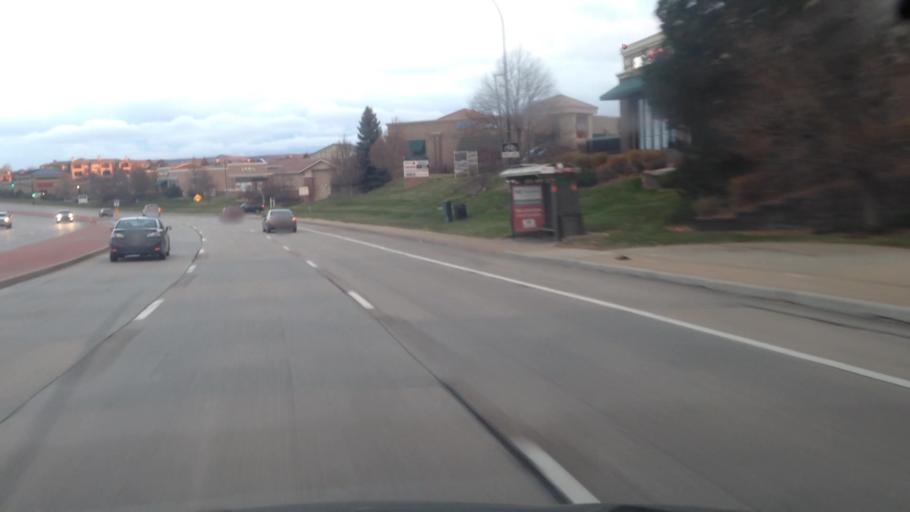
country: US
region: Colorado
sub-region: Douglas County
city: Highlands Ranch
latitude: 39.5435
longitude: -104.9426
